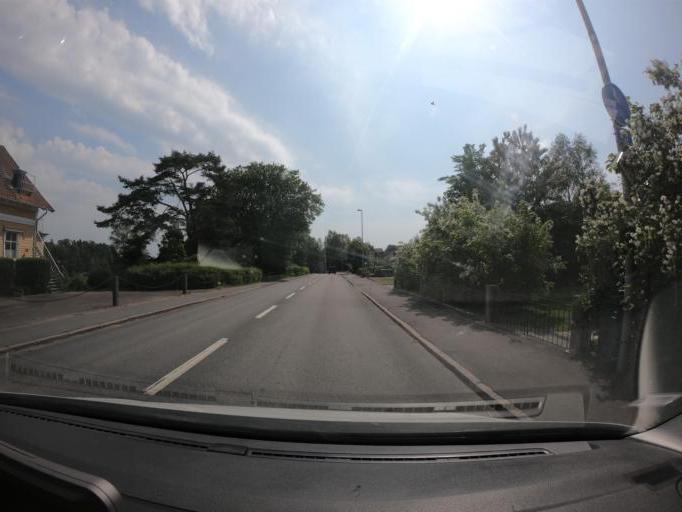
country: SE
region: Skane
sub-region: Hassleholms Kommun
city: Bjarnum
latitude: 56.3462
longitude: 13.6619
